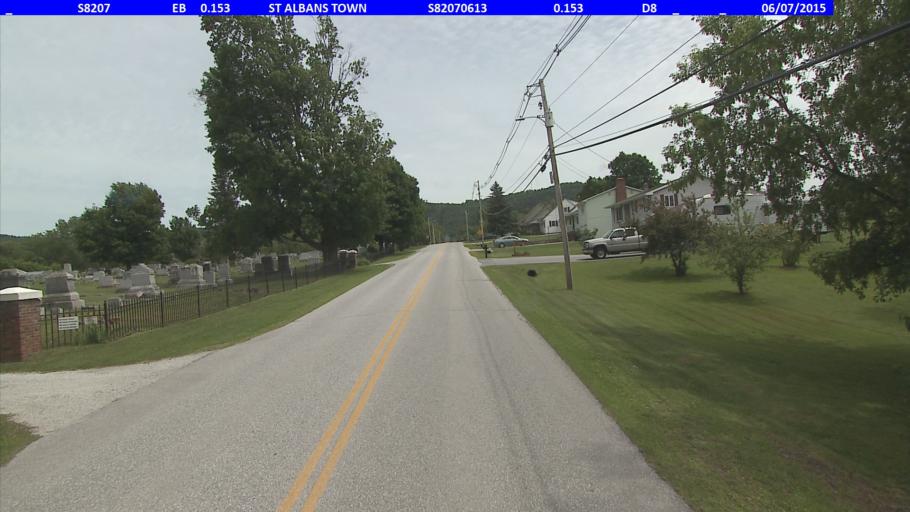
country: US
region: Vermont
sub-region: Franklin County
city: Saint Albans
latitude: 44.7957
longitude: -73.0886
